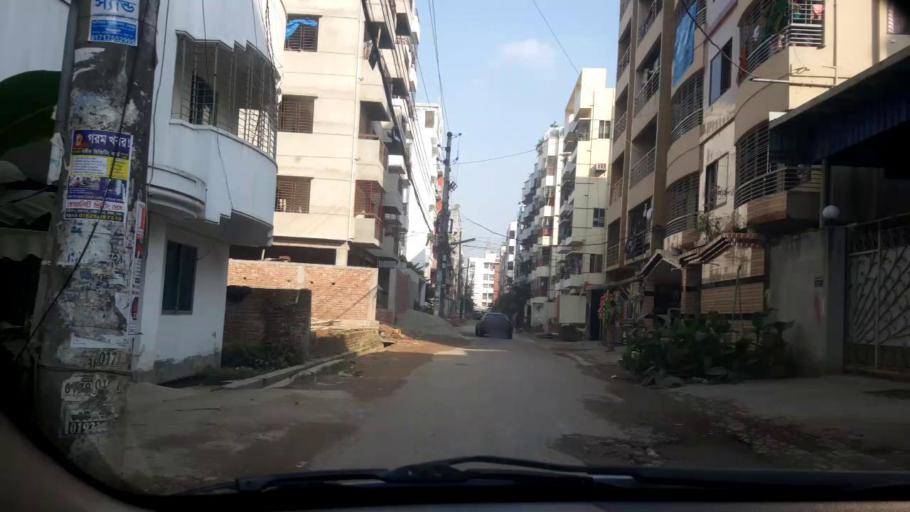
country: BD
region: Dhaka
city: Tungi
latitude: 23.8699
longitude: 90.3811
